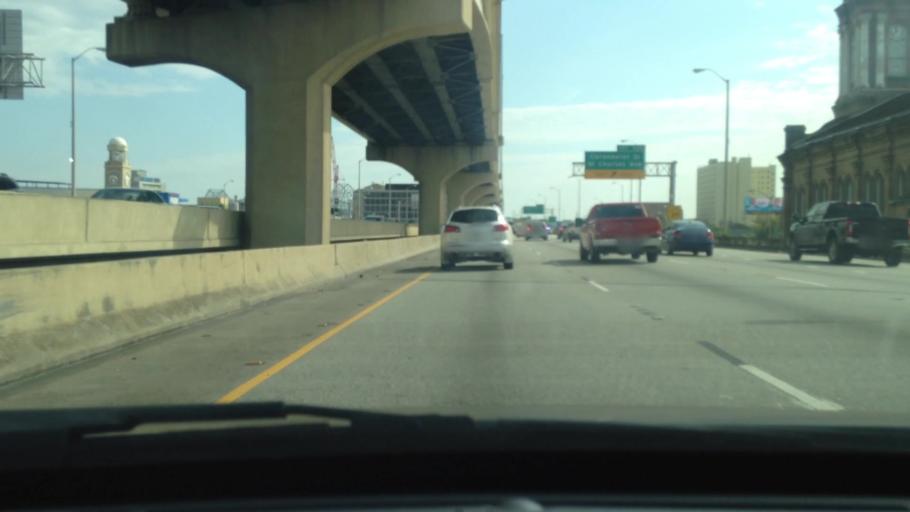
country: US
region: Louisiana
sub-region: Orleans Parish
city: New Orleans
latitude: 29.9448
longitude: -90.0782
